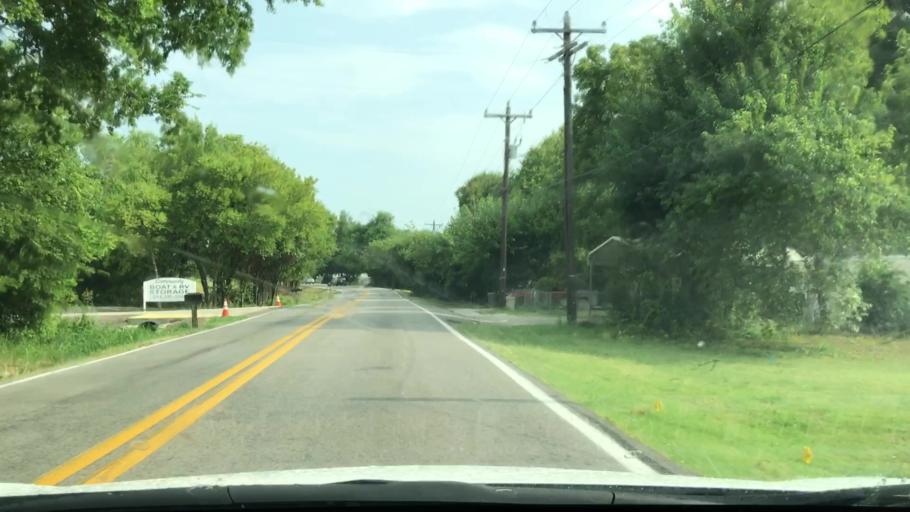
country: US
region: Texas
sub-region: Collin County
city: Wylie
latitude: 32.9768
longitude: -96.5267
